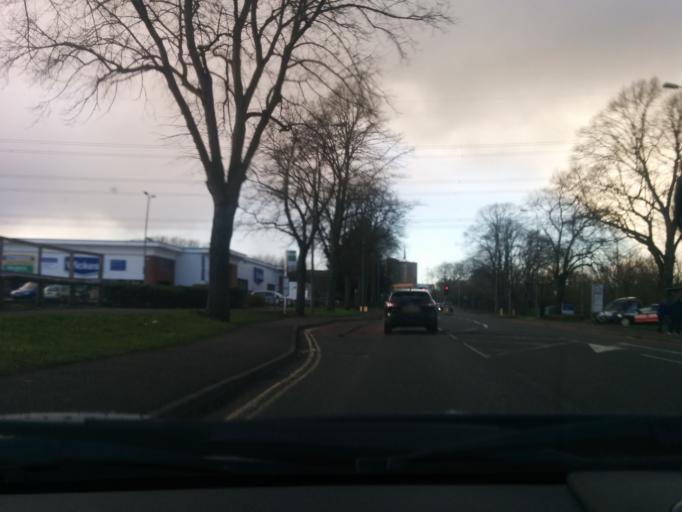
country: GB
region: England
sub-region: Oxfordshire
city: Oxford
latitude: 51.7530
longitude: -1.2881
